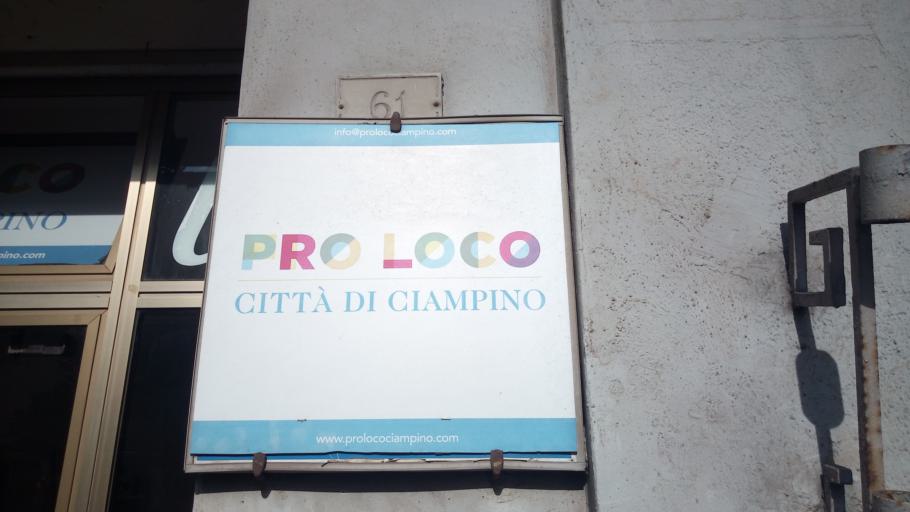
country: IT
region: Latium
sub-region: Citta metropolitana di Roma Capitale
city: Ciampino
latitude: 41.8035
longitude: 12.6007
